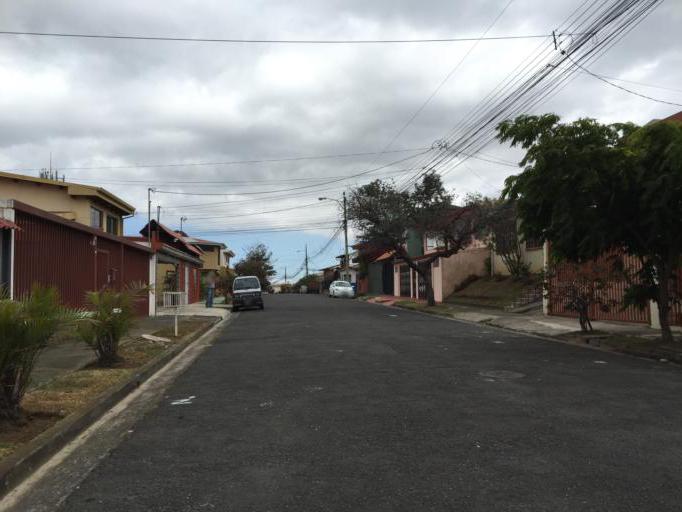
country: CR
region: San Jose
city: San Vicente de Moravia
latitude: 9.9661
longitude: -84.0562
